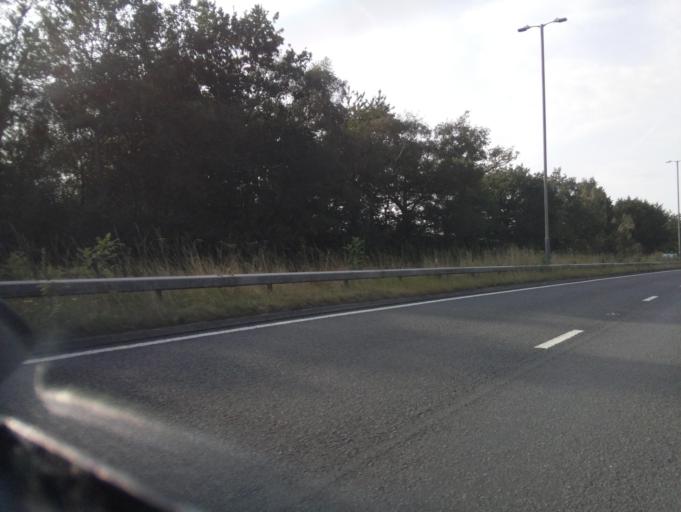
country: GB
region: England
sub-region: Solihull
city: Tidbury Green
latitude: 52.3370
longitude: -1.8731
